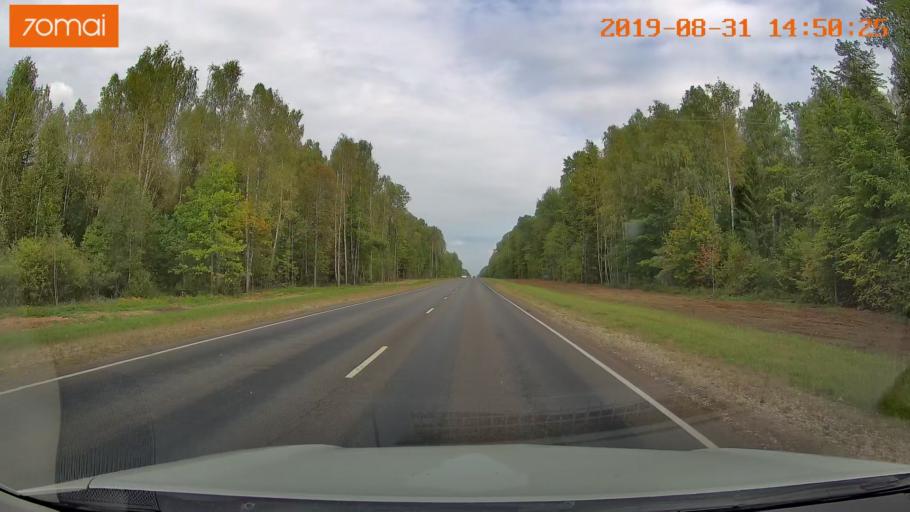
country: RU
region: Kaluga
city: Spas-Demensk
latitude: 54.2612
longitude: 33.7892
